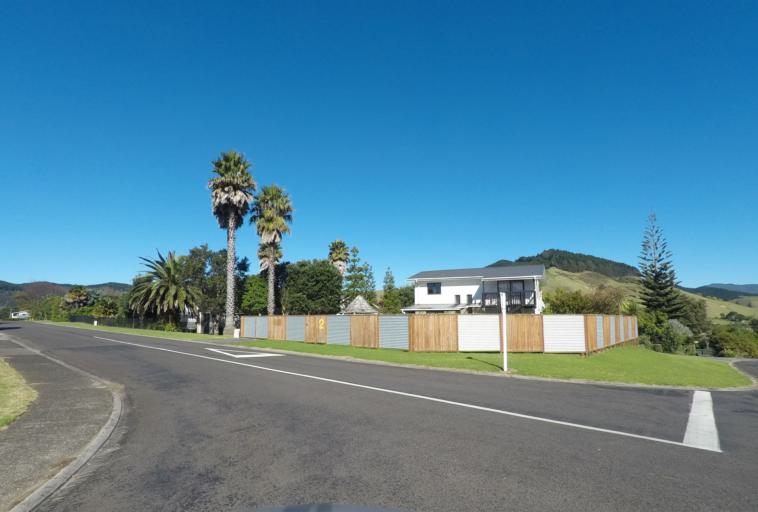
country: NZ
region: Waikato
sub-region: Thames-Coromandel District
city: Whangamata
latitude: -37.2806
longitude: 175.8997
